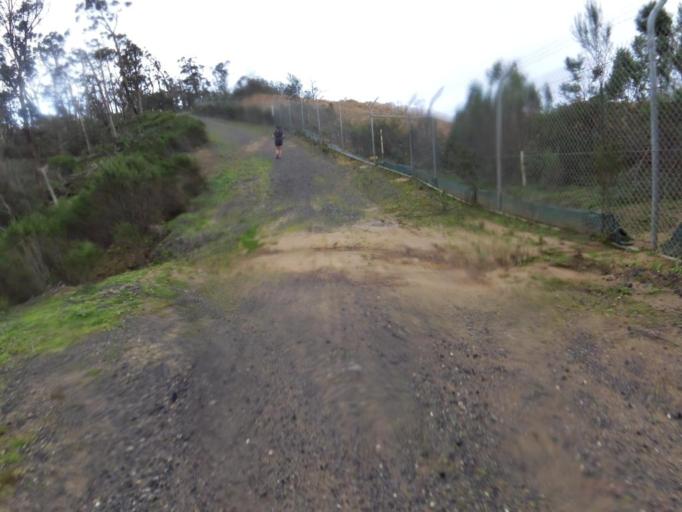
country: AU
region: Victoria
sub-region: Yarra Ranges
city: Lysterfield
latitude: -37.9348
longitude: 145.2762
